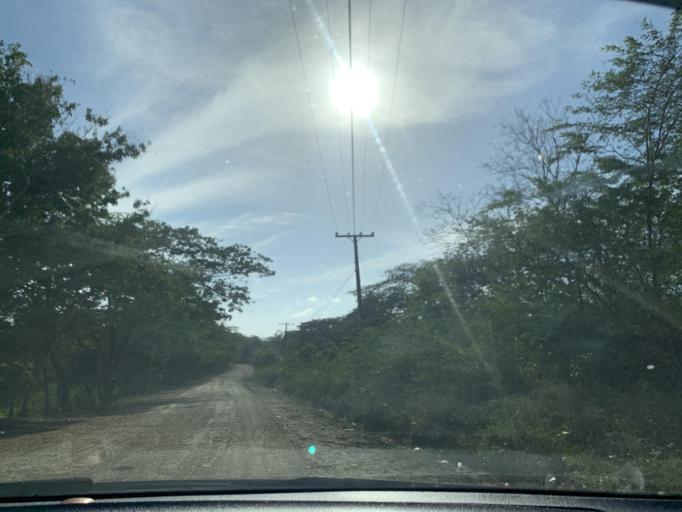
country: DO
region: Puerto Plata
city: Luperon
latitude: 19.8789
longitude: -70.9306
